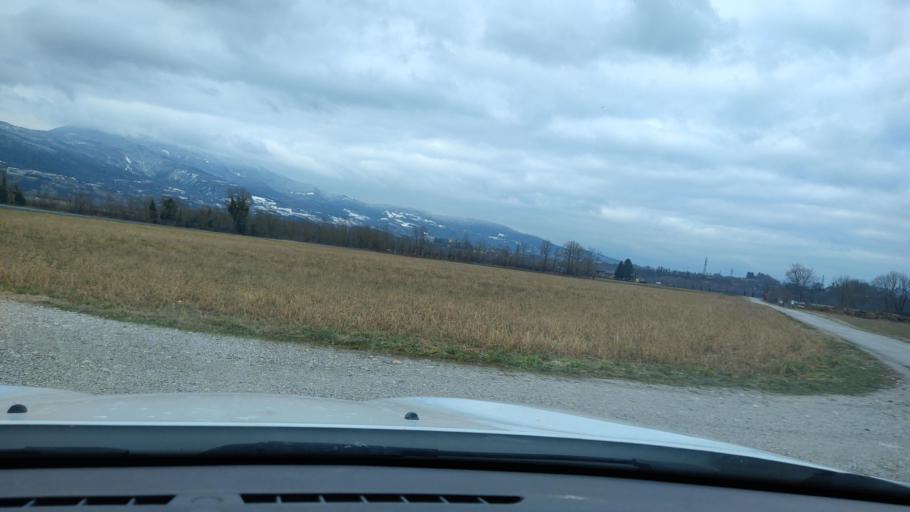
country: FR
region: Rhone-Alpes
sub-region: Departement de la Savoie
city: Montmelian
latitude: 45.4857
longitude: 6.0343
